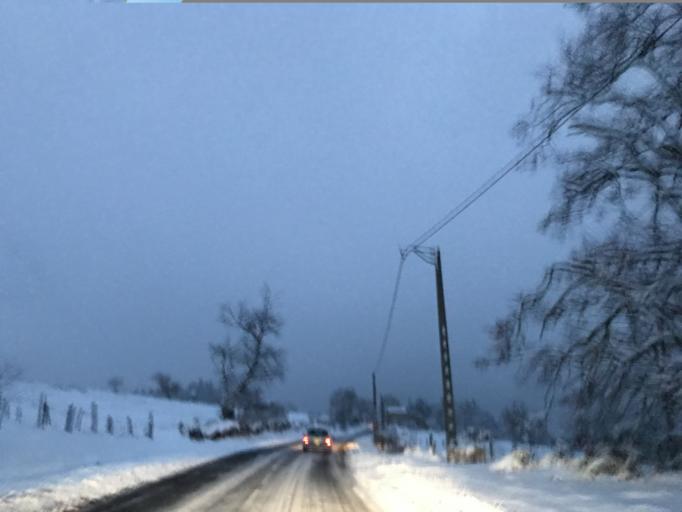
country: FR
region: Auvergne
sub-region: Departement du Puy-de-Dome
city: Courpiere
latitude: 45.7184
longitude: 3.5891
